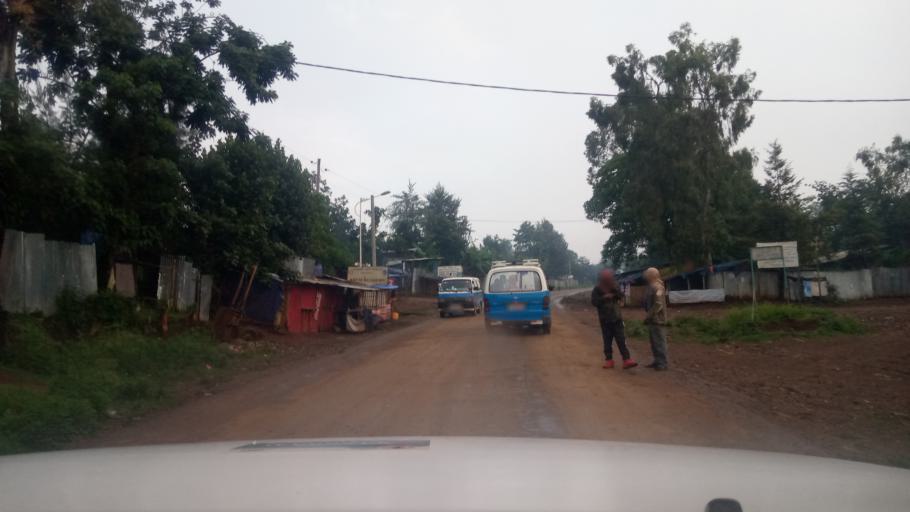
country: ET
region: Oromiya
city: Jima
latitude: 7.6948
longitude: 36.8179
